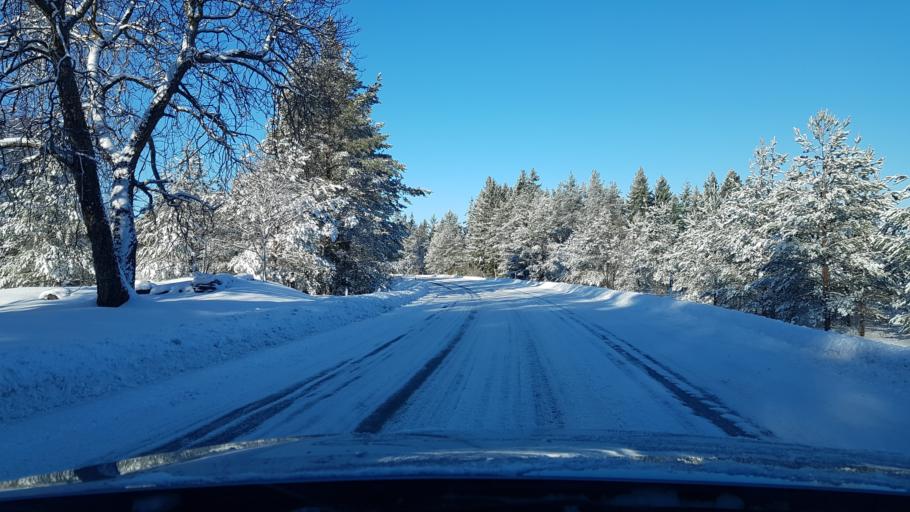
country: EE
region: Hiiumaa
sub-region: Kaerdla linn
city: Kardla
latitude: 58.9354
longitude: 22.7820
